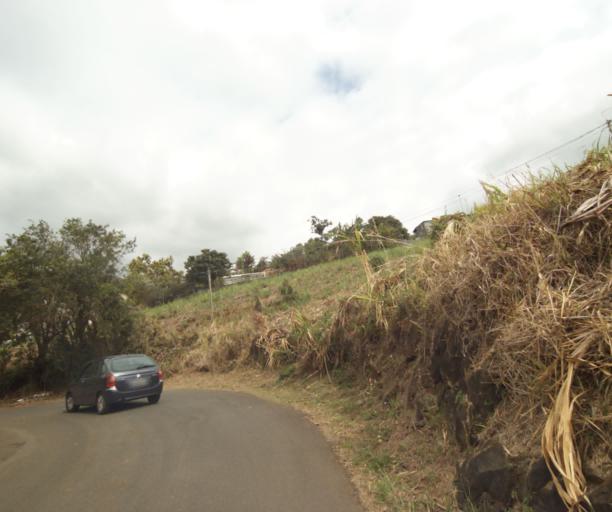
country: RE
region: Reunion
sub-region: Reunion
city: Saint-Paul
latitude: -21.0305
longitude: 55.2985
